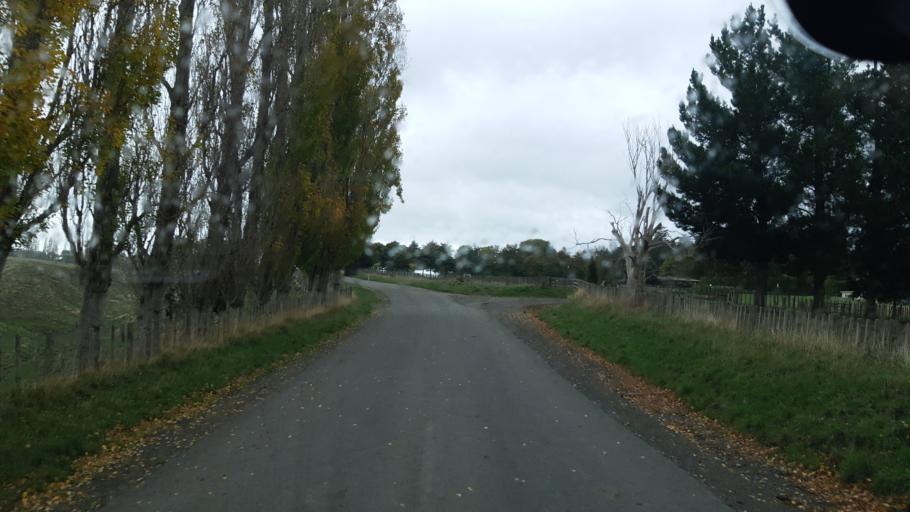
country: NZ
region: Manawatu-Wanganui
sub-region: Ruapehu District
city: Waiouru
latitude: -39.6204
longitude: 175.6232
